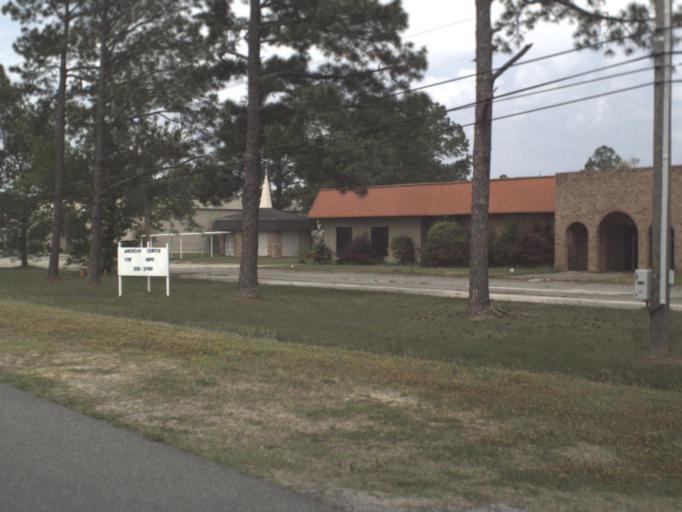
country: US
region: Florida
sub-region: Escambia County
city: Myrtle Grove
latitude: 30.4032
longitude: -87.3270
